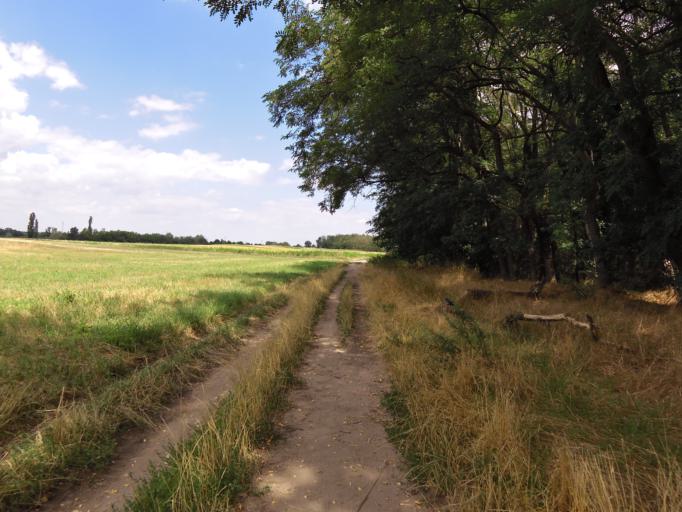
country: DE
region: Rheinland-Pfalz
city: Birkenheide
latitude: 49.4848
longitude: 8.2580
